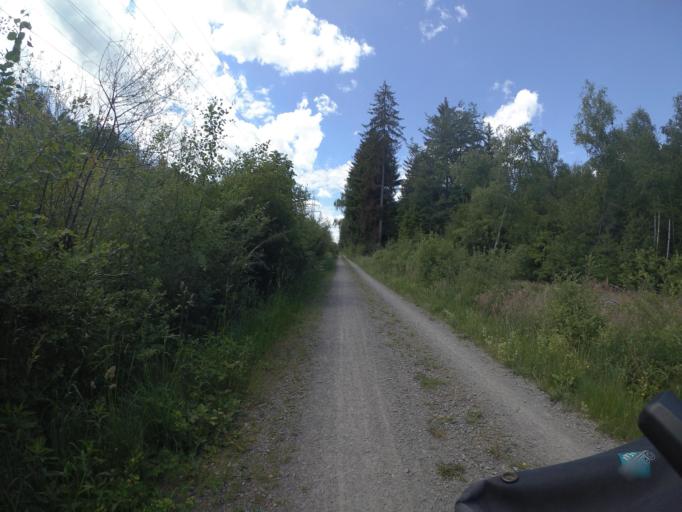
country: DE
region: Rheinland-Pfalz
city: Landstuhl
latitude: 49.4151
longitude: 7.5428
